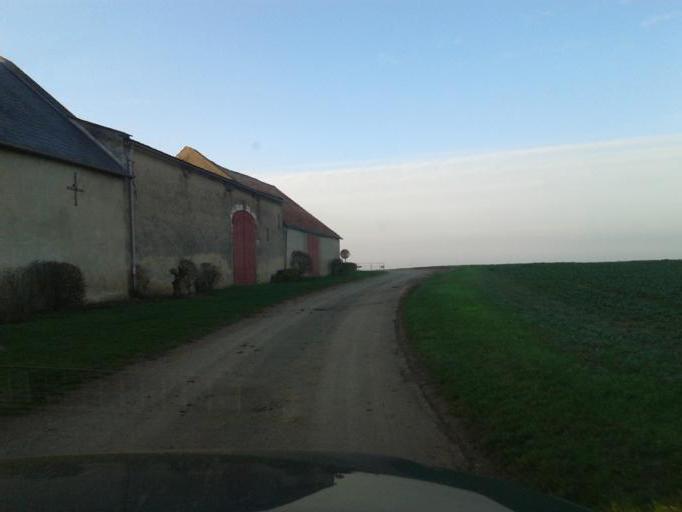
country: FR
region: Centre
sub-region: Departement du Loiret
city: Tavers
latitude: 47.7684
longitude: 1.5818
